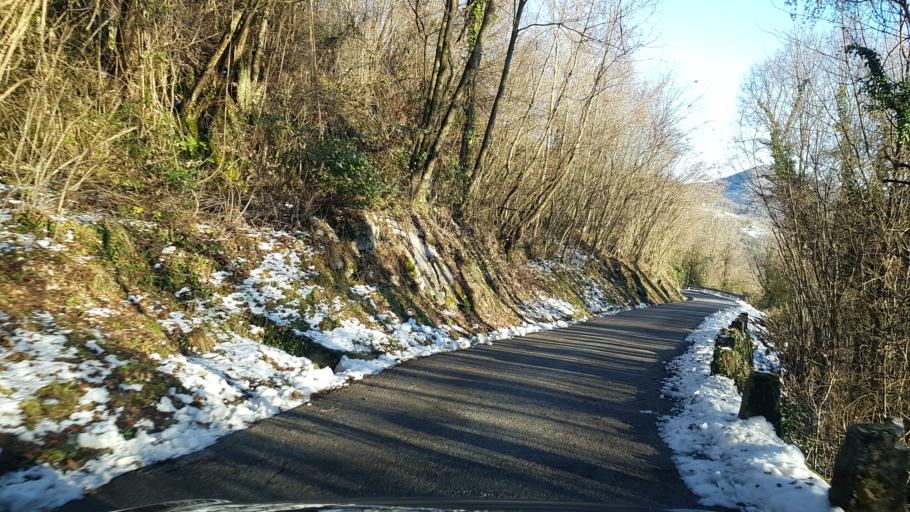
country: IT
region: Friuli Venezia Giulia
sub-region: Provincia di Udine
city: Savogna
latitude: 46.1870
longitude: 13.5285
